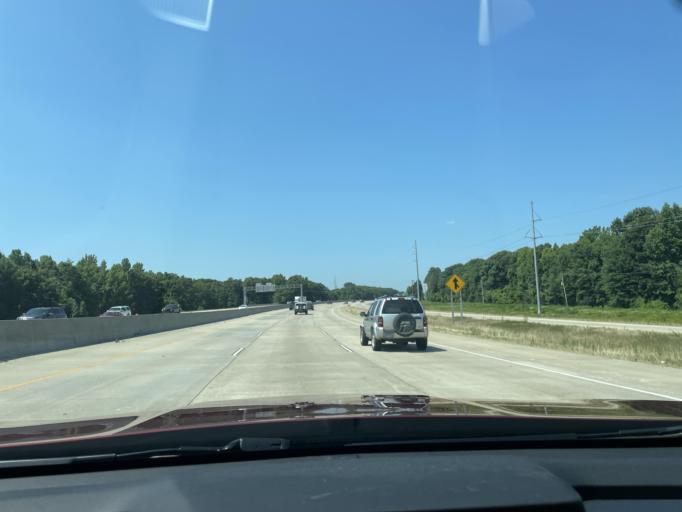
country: US
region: Arkansas
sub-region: Pulaski County
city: Jacksonville
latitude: 34.8592
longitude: -92.1314
